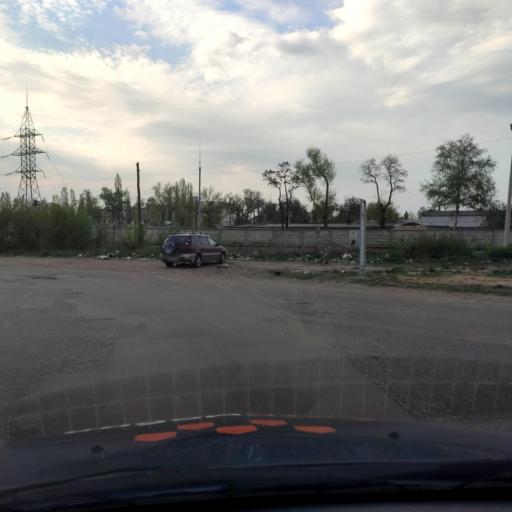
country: RU
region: Voronezj
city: Voronezh
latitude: 51.6466
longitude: 39.2689
